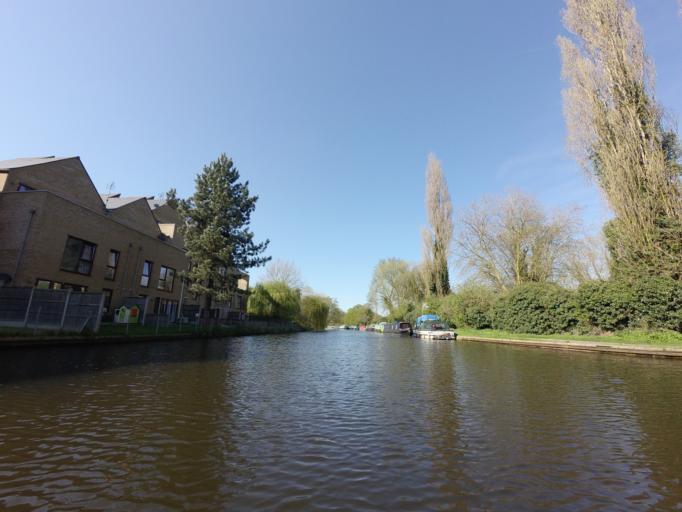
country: GB
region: England
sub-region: Greater London
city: Uxbridge
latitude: 51.5529
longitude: -0.4836
